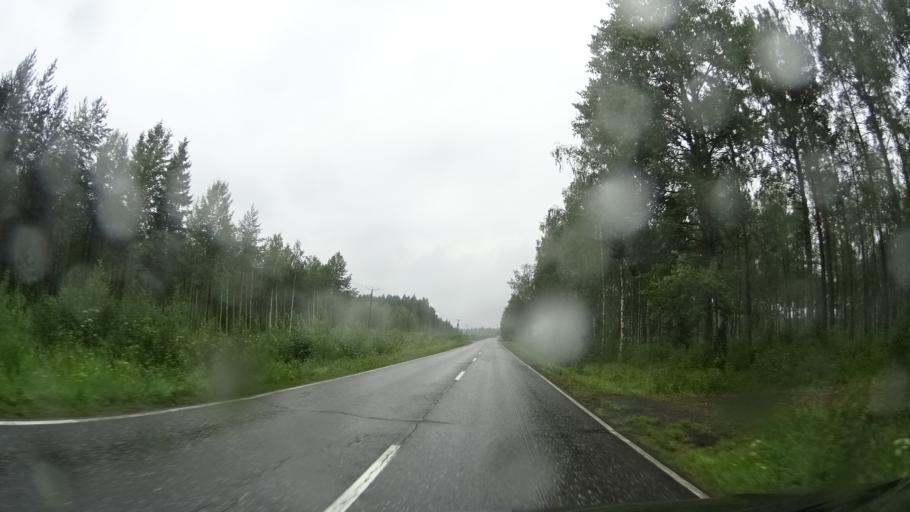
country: FI
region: North Karelia
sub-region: Keski-Karjala
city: Raeaekkylae
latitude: 62.3099
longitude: 29.5264
